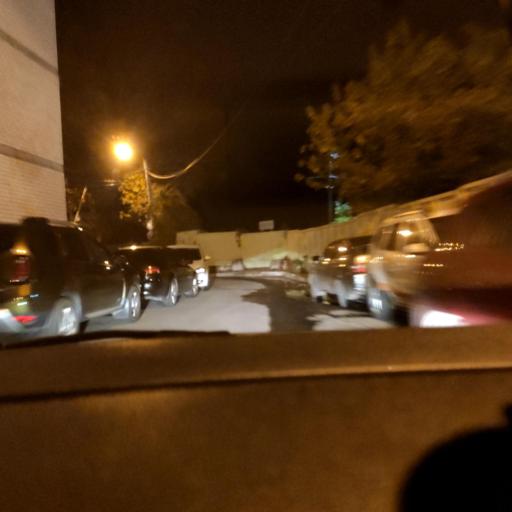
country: RU
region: Voronezj
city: Voronezh
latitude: 51.7118
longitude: 39.2035
